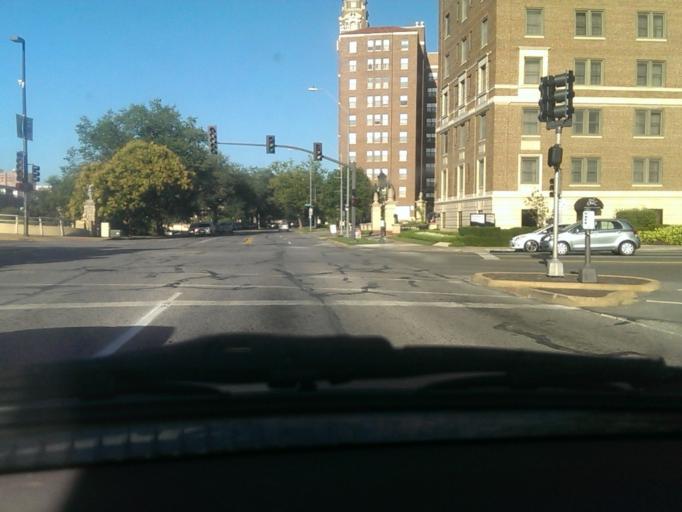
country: US
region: Kansas
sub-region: Johnson County
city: Westwood
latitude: 39.0398
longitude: -94.5921
